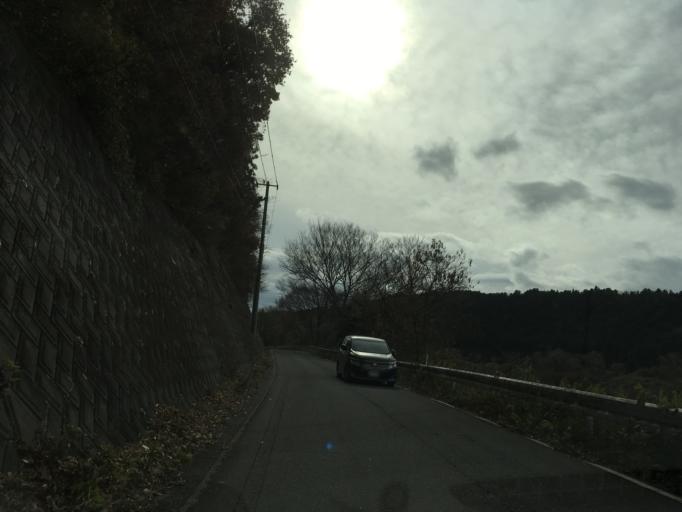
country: JP
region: Iwate
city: Ichinoseki
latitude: 38.7747
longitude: 141.2681
